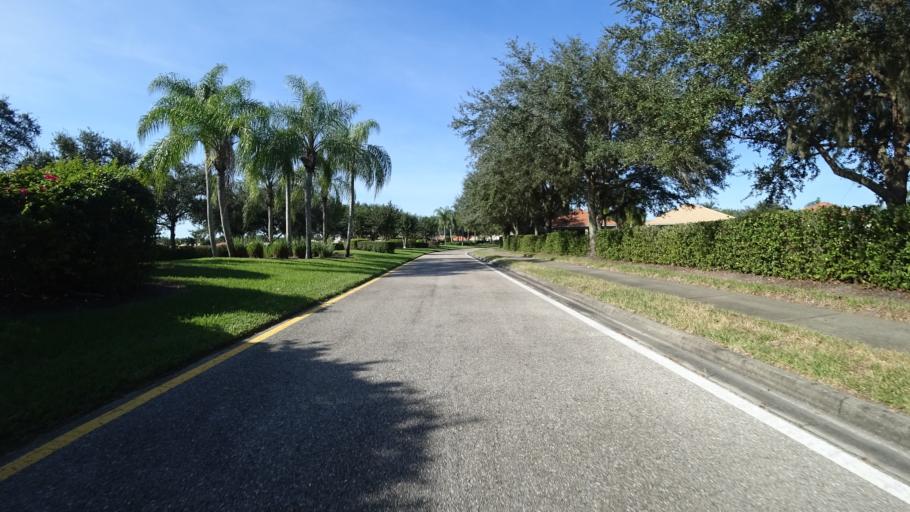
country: US
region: Florida
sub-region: Sarasota County
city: Desoto Lakes
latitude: 27.4185
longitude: -82.4653
